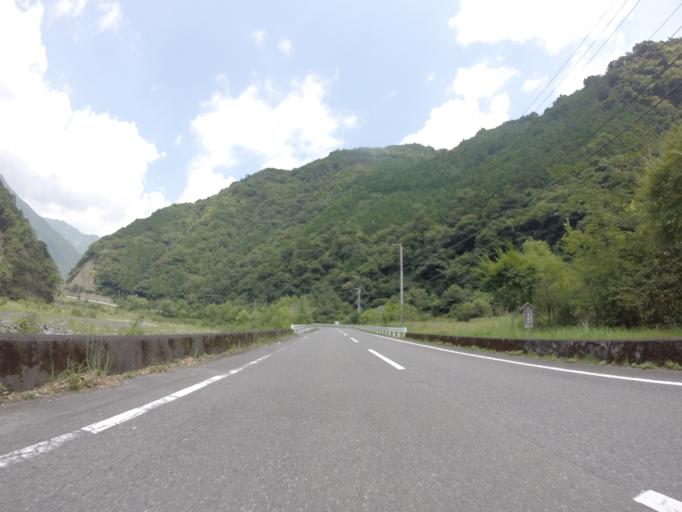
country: JP
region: Shizuoka
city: Shizuoka-shi
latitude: 35.2511
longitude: 138.3395
